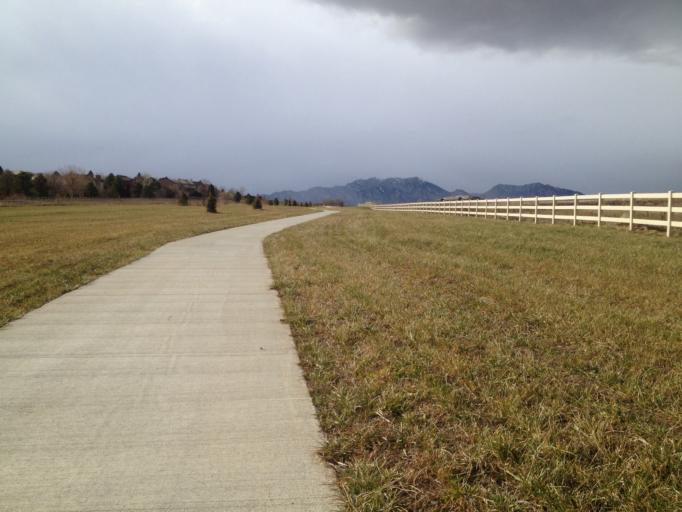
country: US
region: Colorado
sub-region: Boulder County
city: Superior
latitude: 39.9474
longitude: -105.1549
